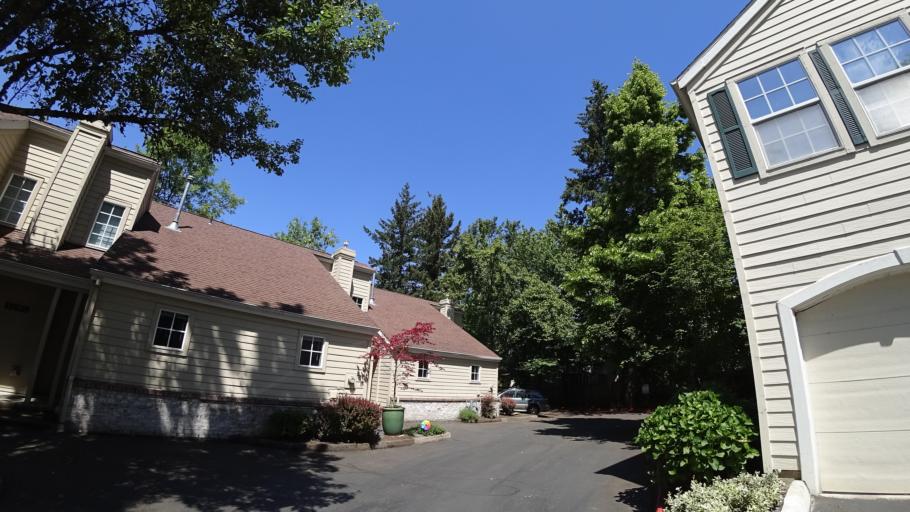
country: US
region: Oregon
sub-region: Washington County
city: King City
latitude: 45.4383
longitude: -122.8130
